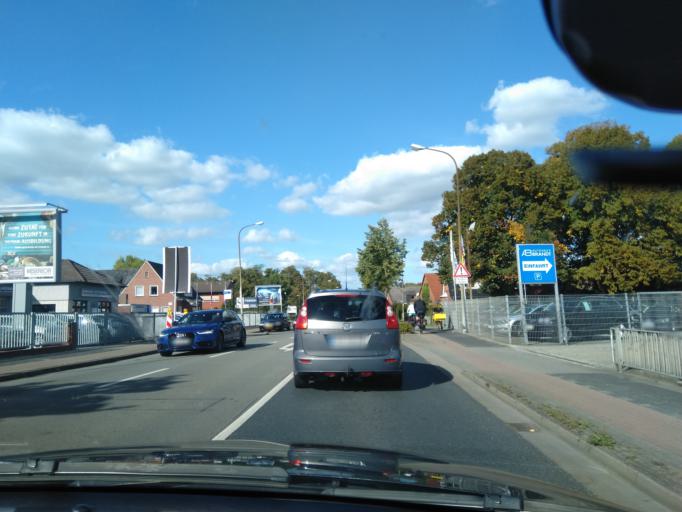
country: DE
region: Lower Saxony
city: Leer
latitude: 53.2442
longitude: 7.4572
